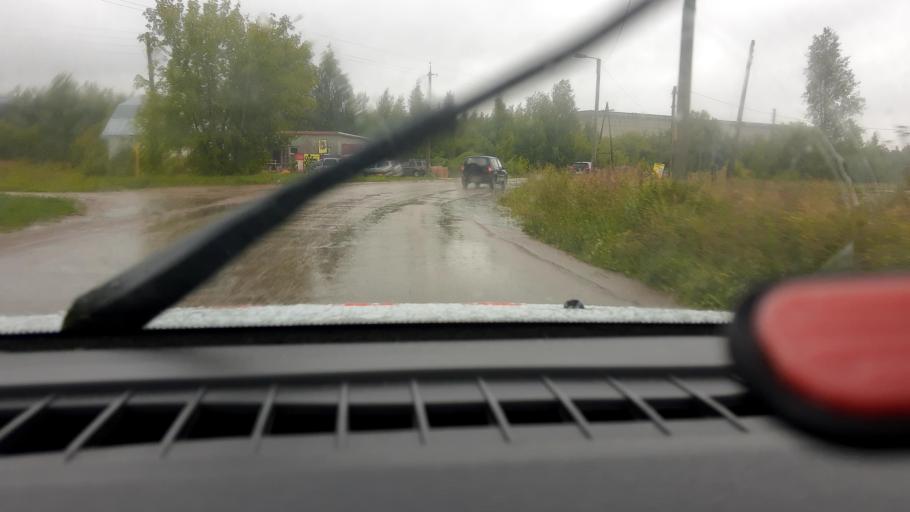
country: RU
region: Nizjnij Novgorod
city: Lyskovo
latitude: 56.0275
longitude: 45.0300
